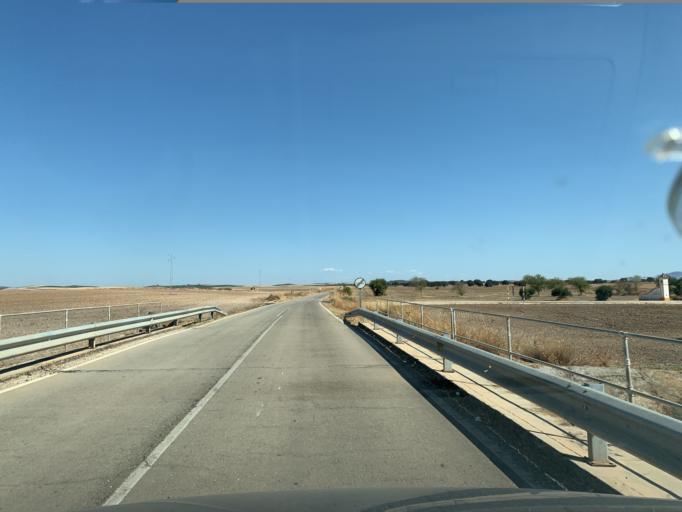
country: ES
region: Andalusia
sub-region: Provincia de Sevilla
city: La Lantejuela
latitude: 37.3747
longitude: -5.1530
